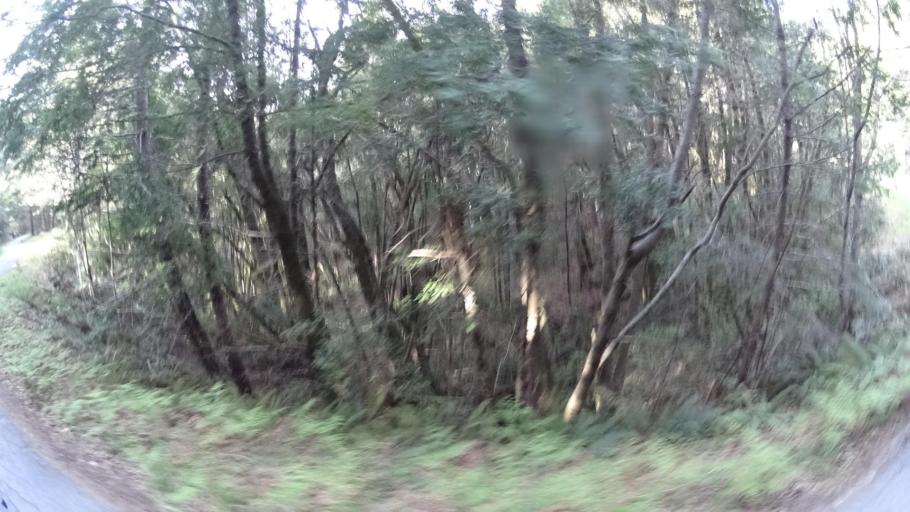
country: US
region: California
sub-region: Humboldt County
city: Hydesville
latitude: 40.6701
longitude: -123.9261
